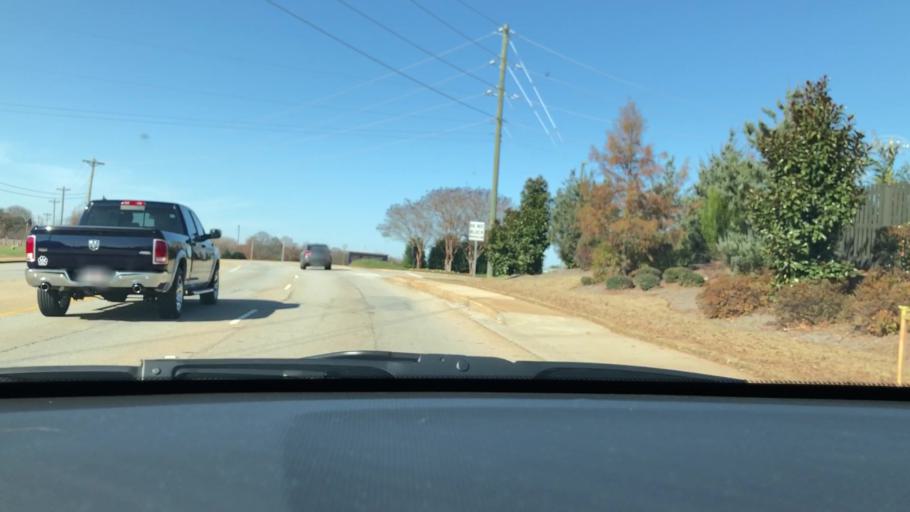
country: US
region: South Carolina
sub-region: Greenville County
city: Five Forks
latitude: 34.8192
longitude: -82.2515
